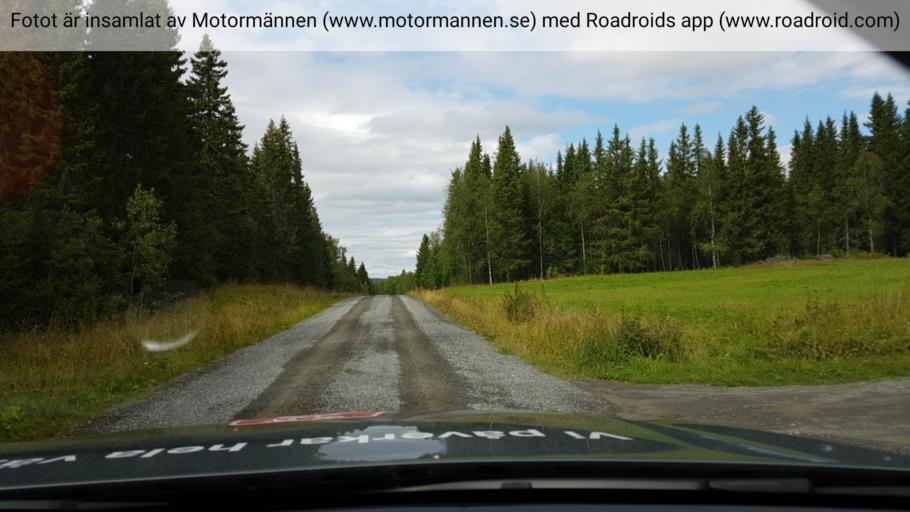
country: SE
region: Jaemtland
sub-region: Krokoms Kommun
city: Valla
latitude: 63.5293
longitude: 13.8794
